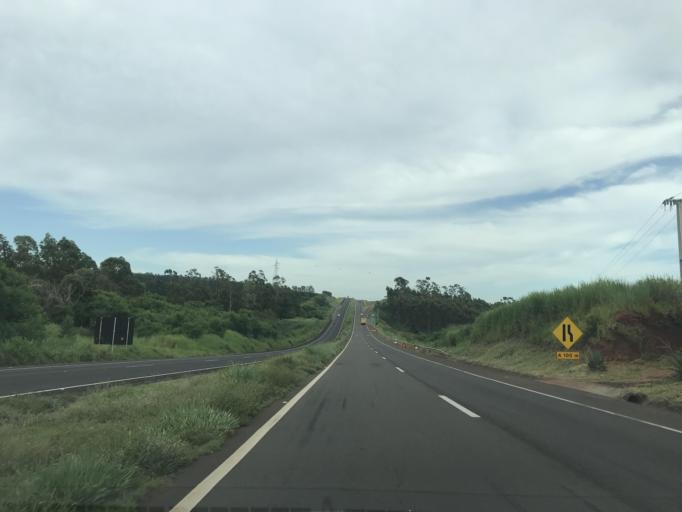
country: BR
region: Parana
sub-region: Alto Parana
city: Alto Parana
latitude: -23.1144
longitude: -52.3285
